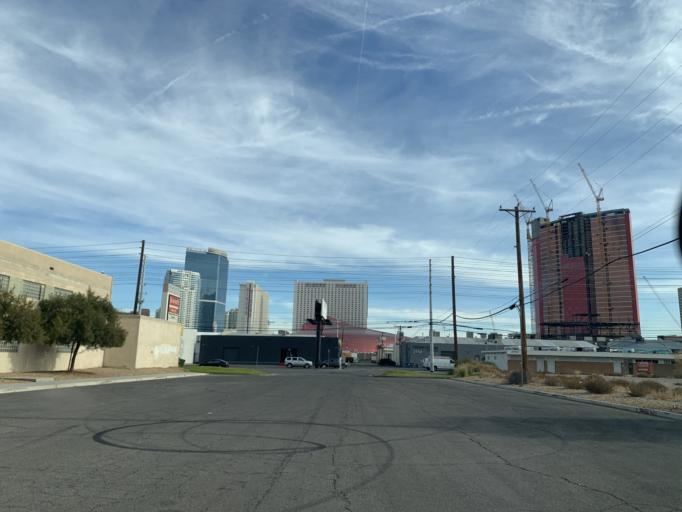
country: US
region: Nevada
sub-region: Clark County
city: Las Vegas
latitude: 36.1404
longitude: -115.1720
